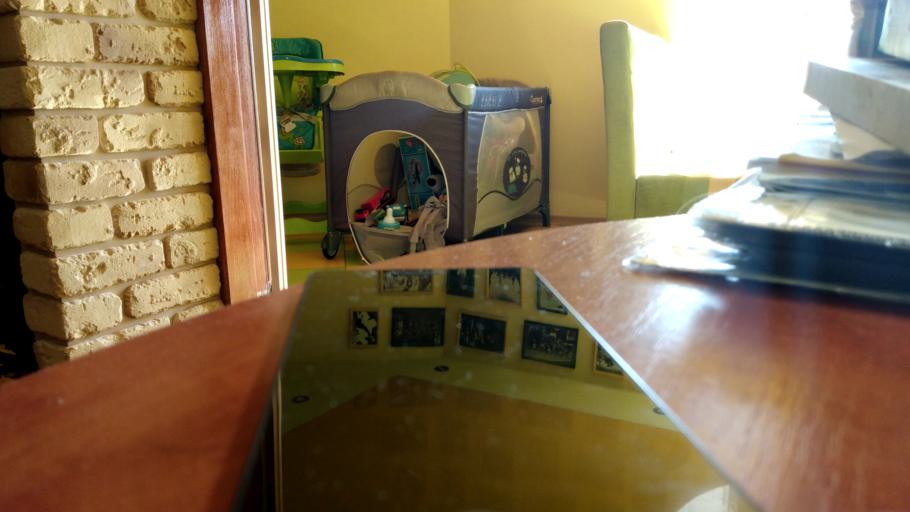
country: RU
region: Saratov
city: Yekaterinovka
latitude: 52.2876
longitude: 44.4069
